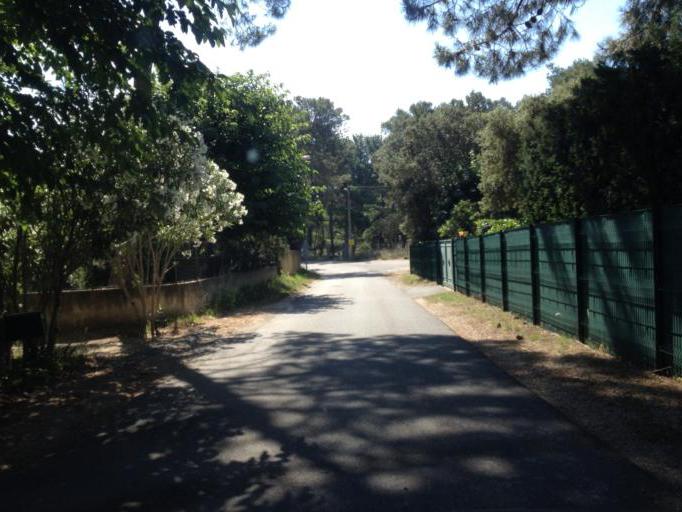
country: FR
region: Provence-Alpes-Cote d'Azur
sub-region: Departement du Vaucluse
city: Mornas
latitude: 44.2131
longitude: 4.7457
